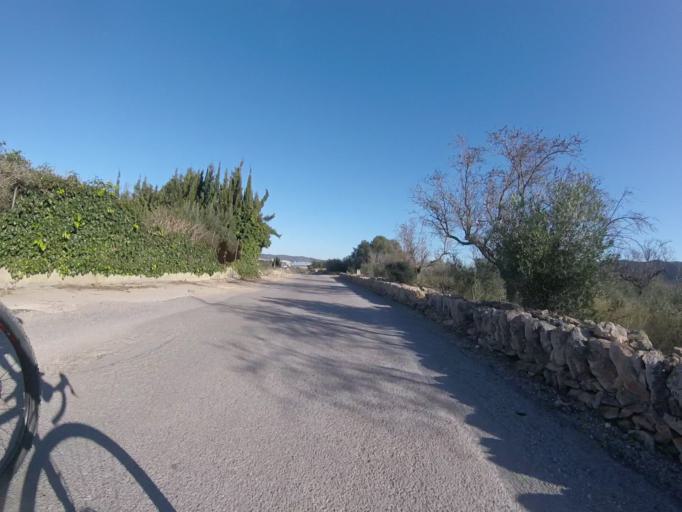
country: ES
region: Valencia
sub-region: Provincia de Castello
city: Alcala de Xivert
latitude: 40.2941
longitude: 0.2188
